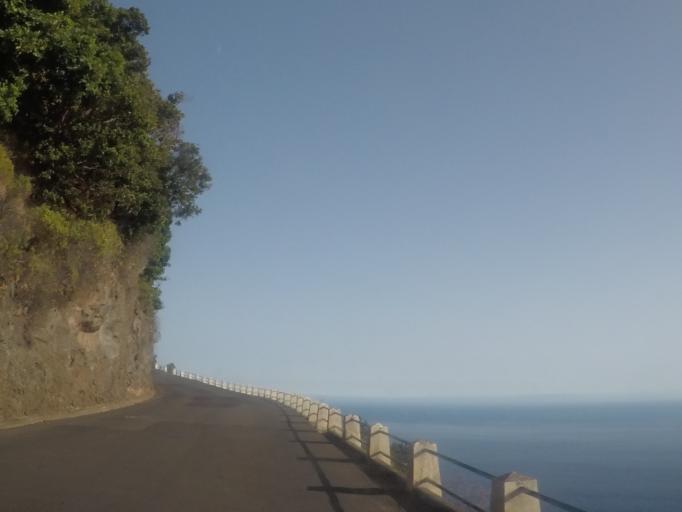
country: PT
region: Madeira
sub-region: Calheta
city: Arco da Calheta
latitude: 32.7077
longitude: -17.1305
